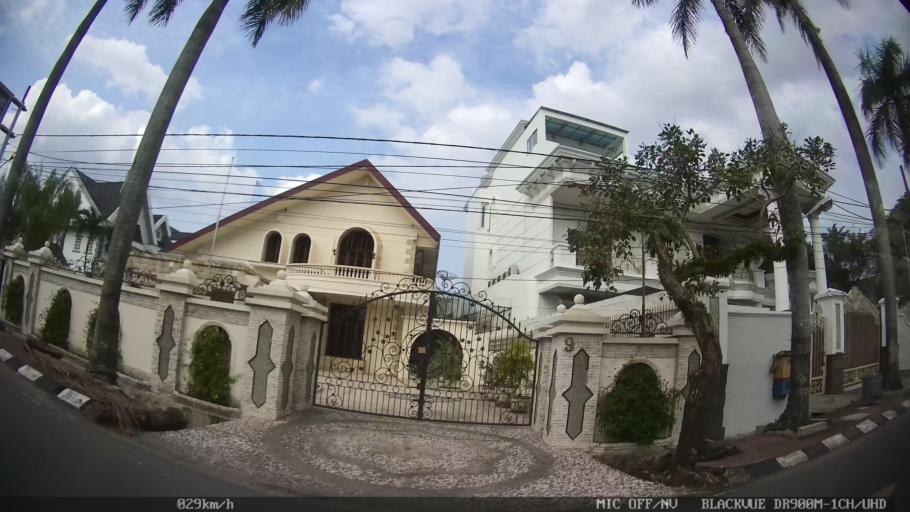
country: ID
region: North Sumatra
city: Medan
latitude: 3.5741
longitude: 98.6707
